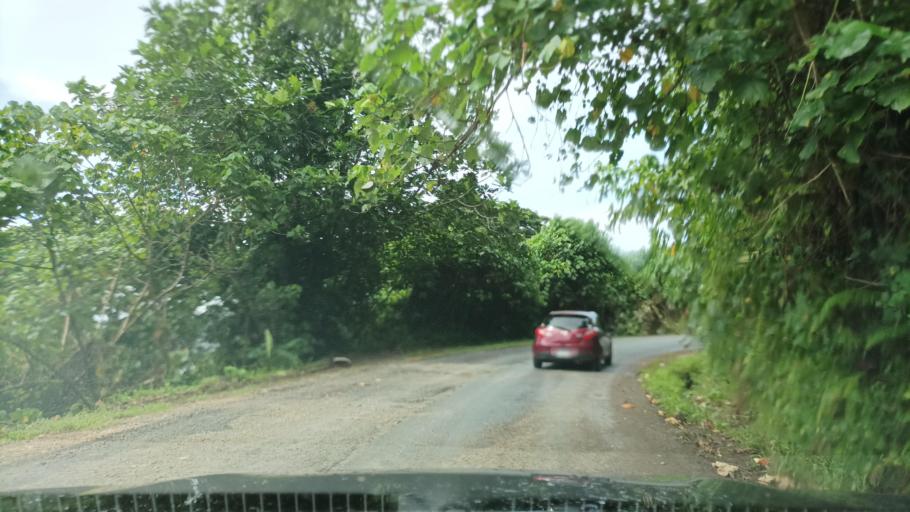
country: FM
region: Pohnpei
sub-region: Madolenihm Municipality
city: Madolenihm Municipality Government
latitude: 6.9164
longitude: 158.3037
